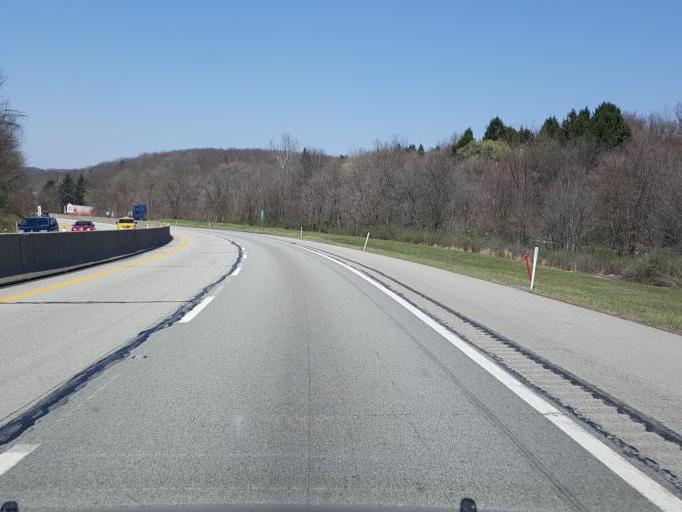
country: US
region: Pennsylvania
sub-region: Westmoreland County
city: Manor
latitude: 40.3802
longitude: -79.6754
